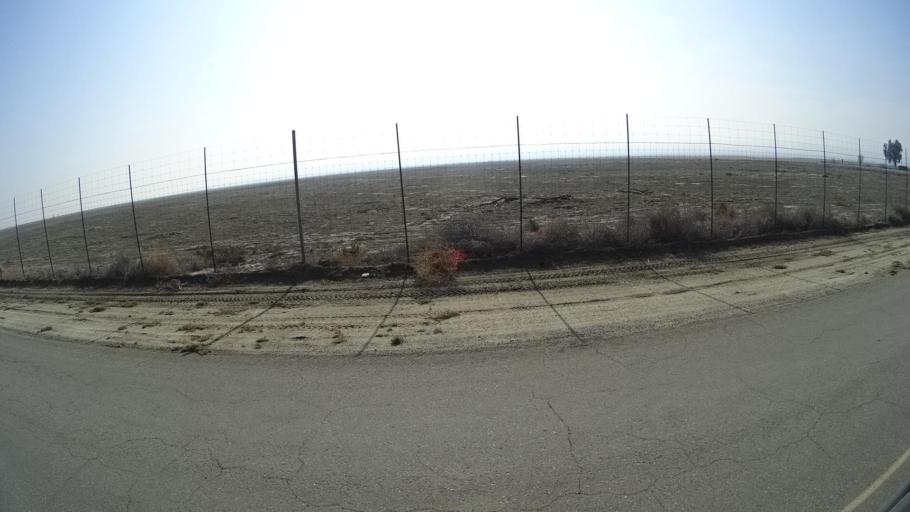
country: US
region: California
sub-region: Kern County
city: Buttonwillow
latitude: 35.3332
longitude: -119.3695
